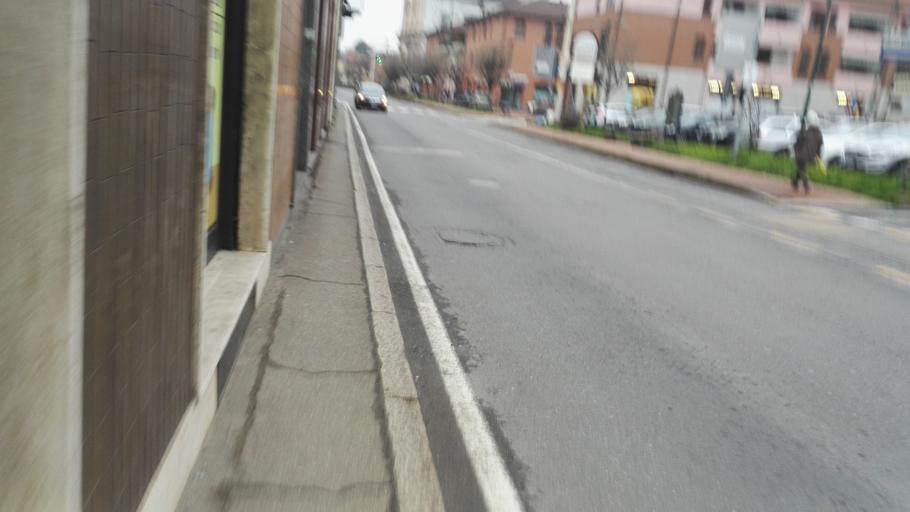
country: IT
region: Lombardy
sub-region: Citta metropolitana di Milano
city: Paderno Dugnano
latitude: 45.5741
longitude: 9.1471
